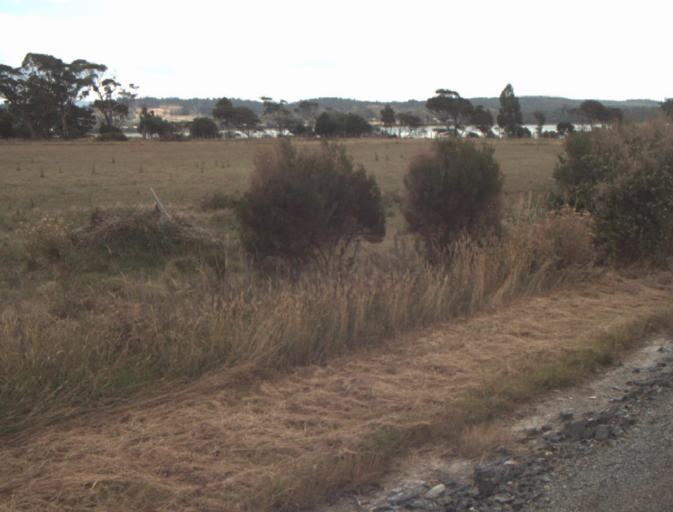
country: AU
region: Tasmania
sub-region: Launceston
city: Mayfield
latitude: -41.2871
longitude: 146.9995
